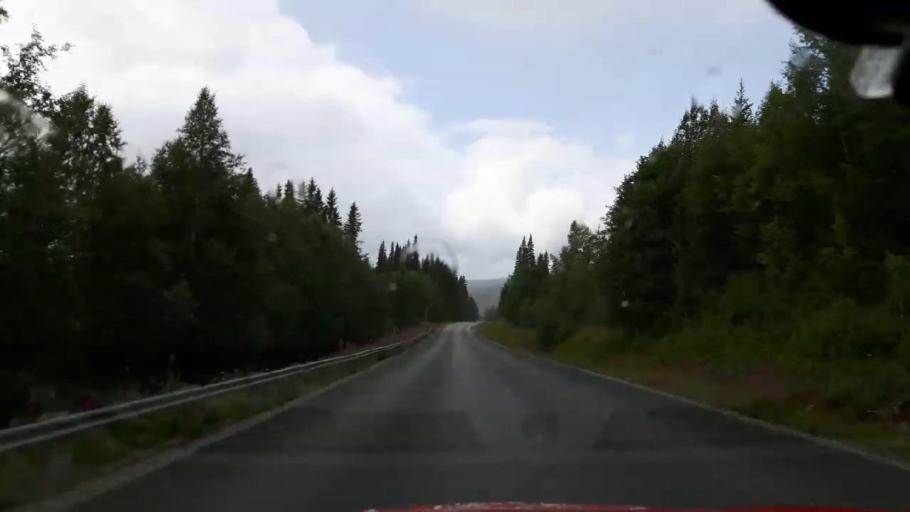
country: SE
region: Vaesterbotten
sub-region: Vilhelmina Kommun
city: Sjoberg
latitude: 64.9431
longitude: 15.7921
